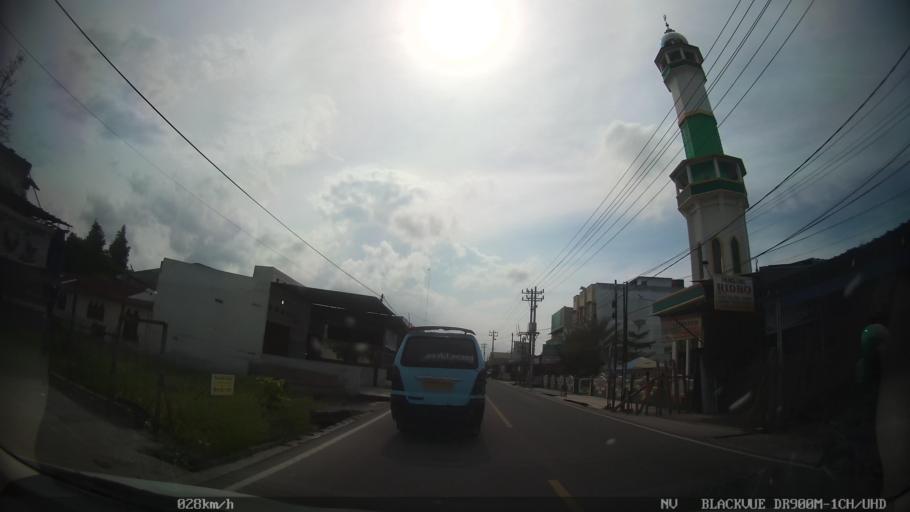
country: ID
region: North Sumatra
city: Percut
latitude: 3.6072
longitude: 98.7673
